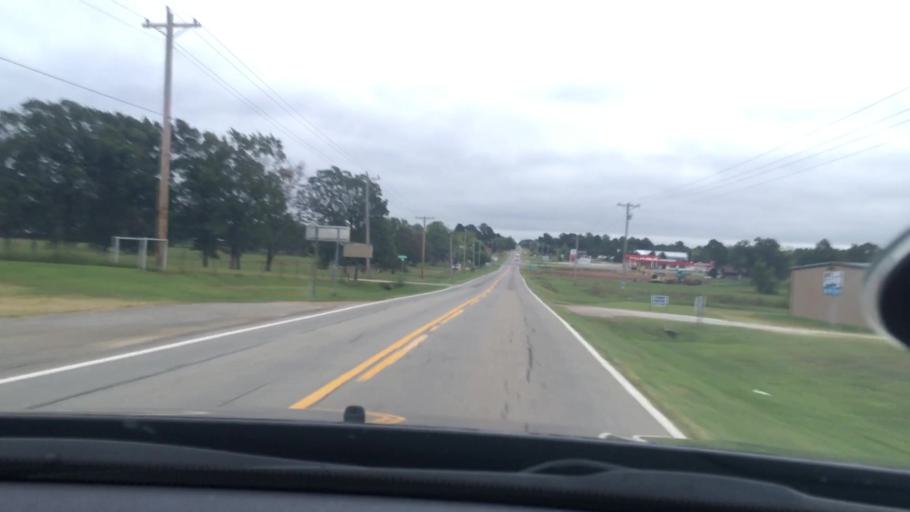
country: US
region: Oklahoma
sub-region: Sequoyah County
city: Vian
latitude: 35.6097
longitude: -94.9807
